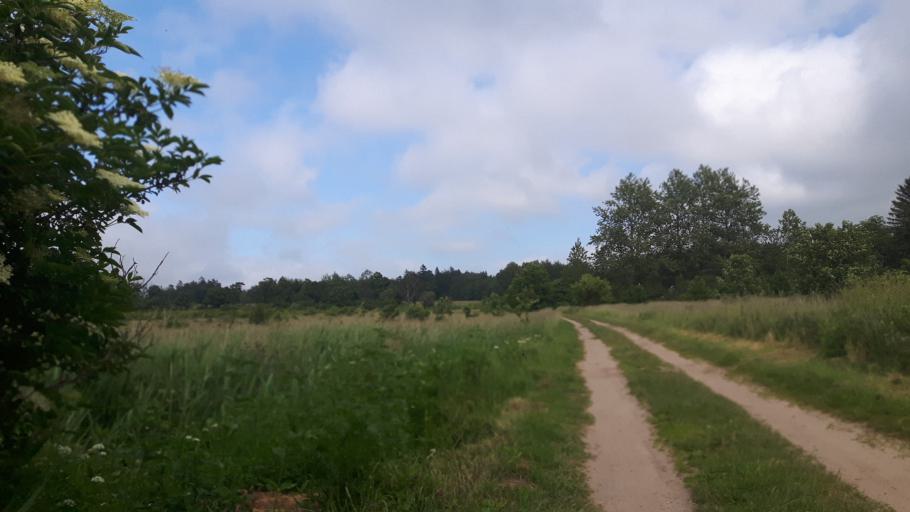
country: PL
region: Pomeranian Voivodeship
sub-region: Slupsk
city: Slupsk
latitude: 54.5999
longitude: 17.0085
